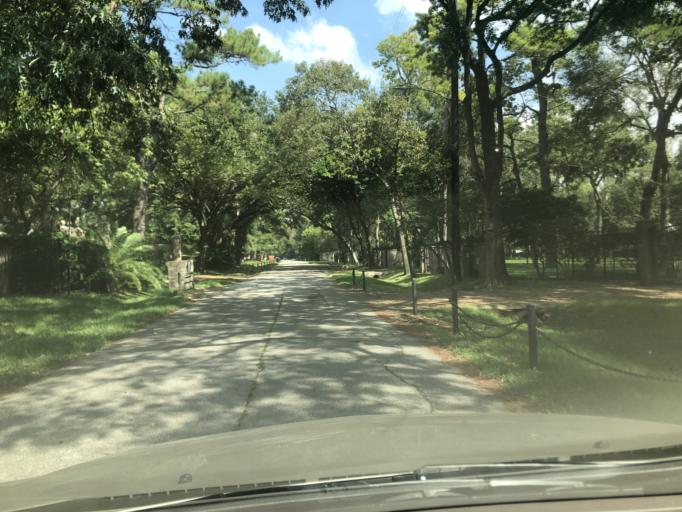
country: US
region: Texas
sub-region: Harris County
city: Bunker Hill Village
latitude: 29.7439
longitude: -95.5417
